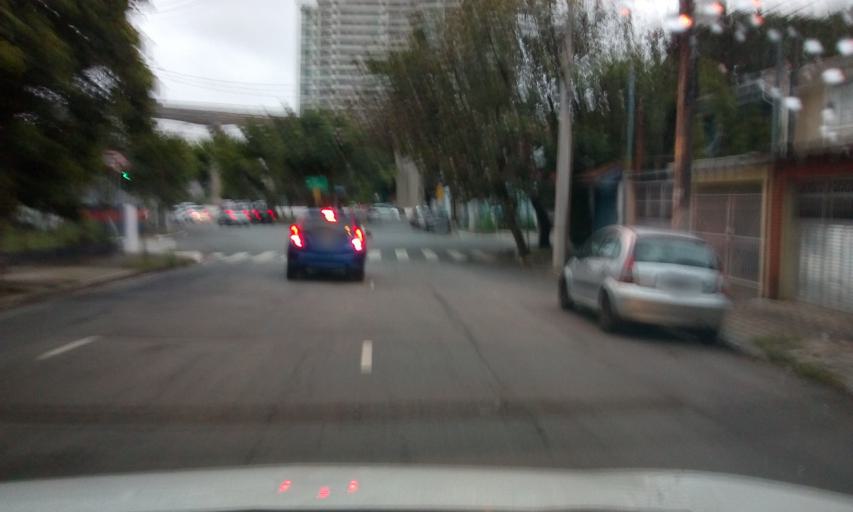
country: BR
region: Sao Paulo
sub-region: Sao Paulo
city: Sao Paulo
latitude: -23.6163
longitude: -46.6903
